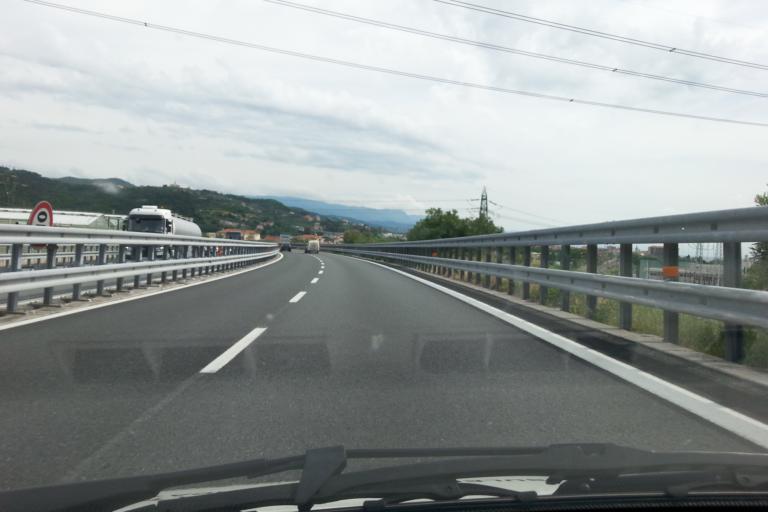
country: IT
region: Liguria
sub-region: Provincia di Savona
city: Valleggia
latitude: 44.2768
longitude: 8.4278
